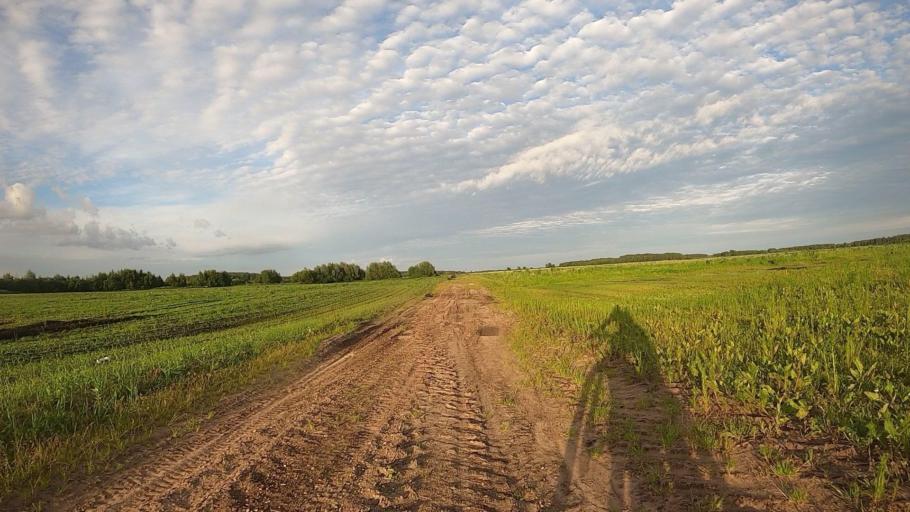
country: LV
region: Olaine
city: Olaine
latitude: 56.8667
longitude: 23.9623
